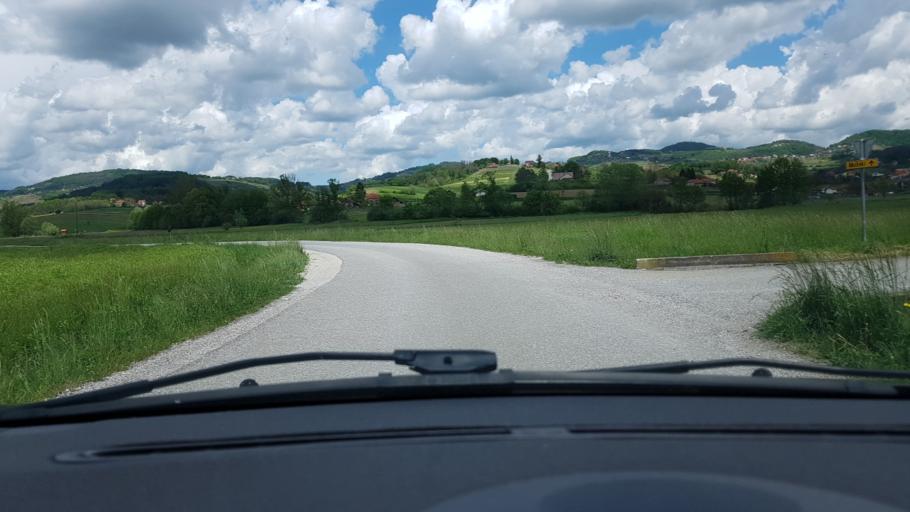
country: HR
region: Krapinsko-Zagorska
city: Pregrada
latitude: 46.1504
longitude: 15.8045
